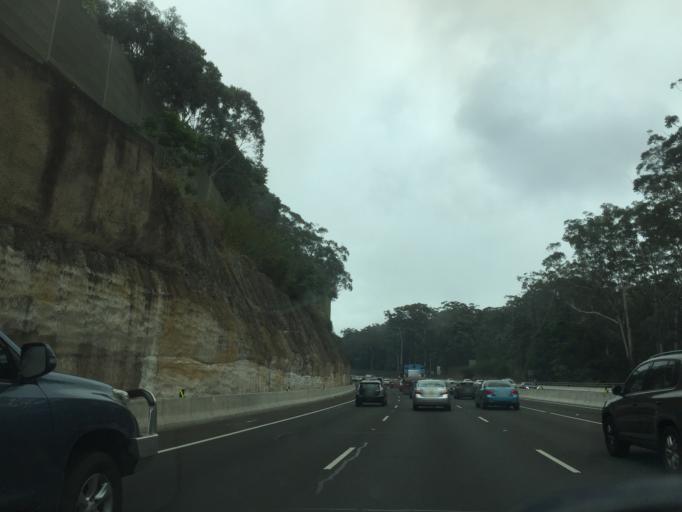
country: AU
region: New South Wales
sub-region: Hornsby Shire
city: Beecroft
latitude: -33.7581
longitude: 151.0646
